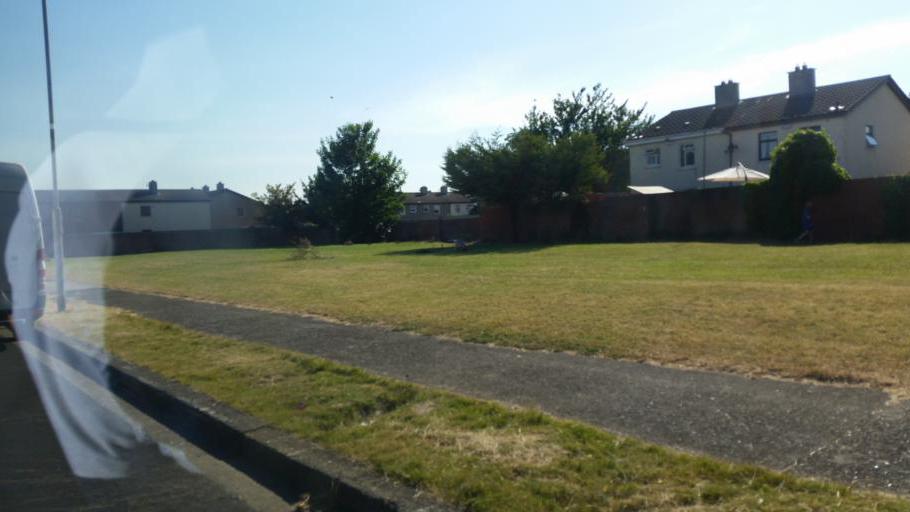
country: IE
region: Leinster
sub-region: Fingal County
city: Blanchardstown
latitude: 53.4017
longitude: -6.3721
